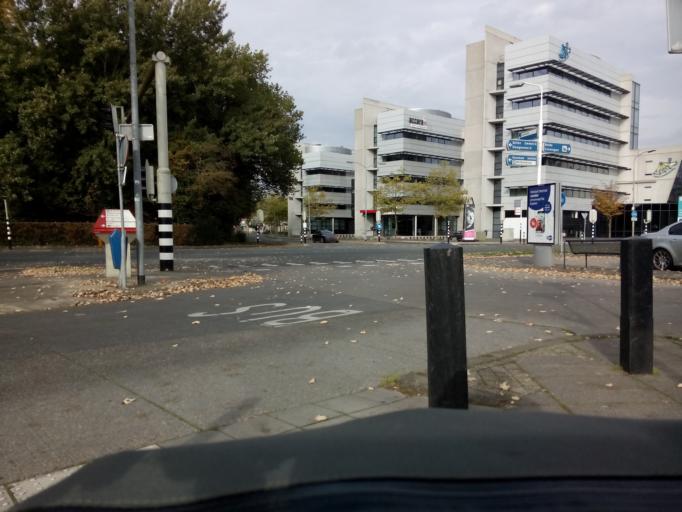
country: NL
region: Drenthe
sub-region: Gemeente Assen
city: Assen
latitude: 52.9920
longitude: 6.5706
